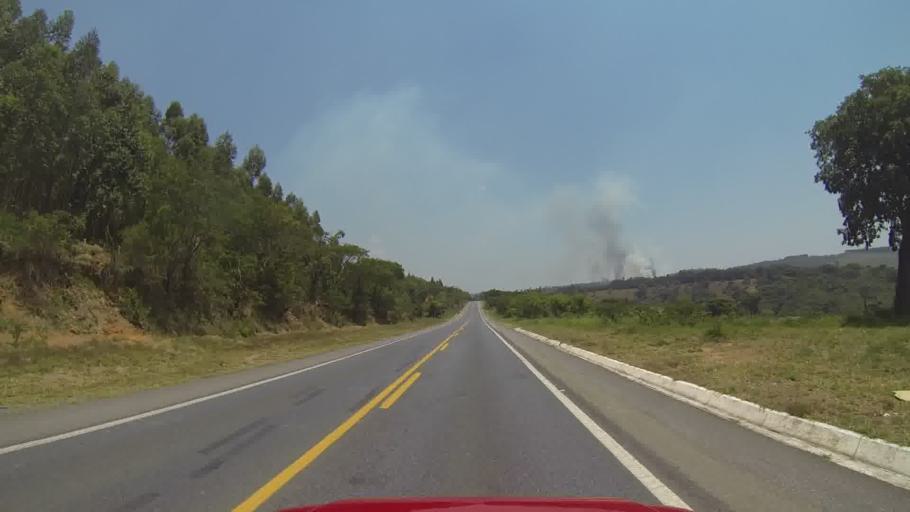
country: BR
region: Minas Gerais
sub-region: Itapecerica
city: Itapecerica
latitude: -20.3429
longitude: -45.2572
